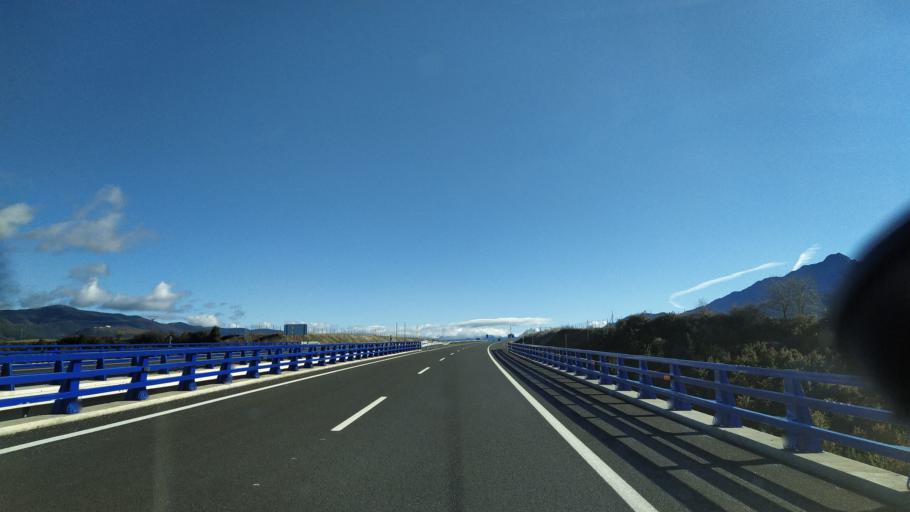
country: ES
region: Aragon
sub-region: Provincia de Huesca
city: Santa Cruz de la Seros
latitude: 42.5639
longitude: -0.6251
